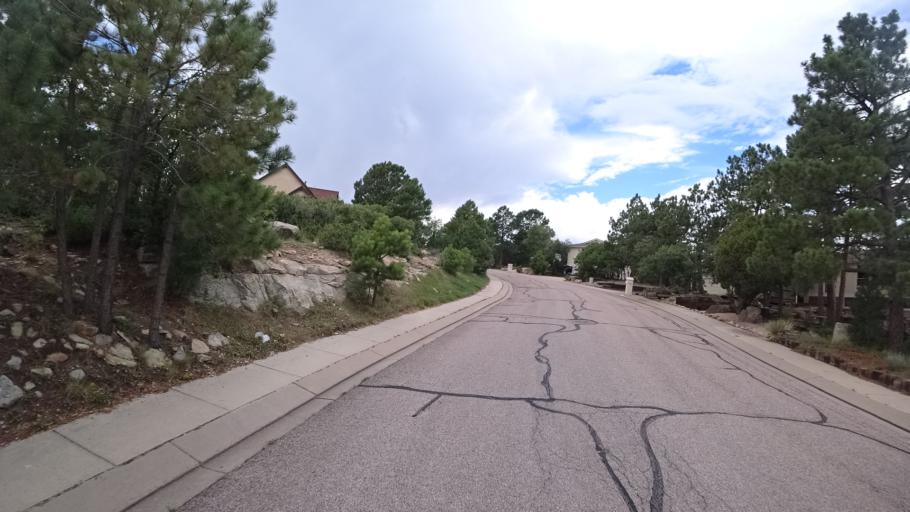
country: US
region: Colorado
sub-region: El Paso County
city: Colorado Springs
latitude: 38.9052
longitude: -104.8469
